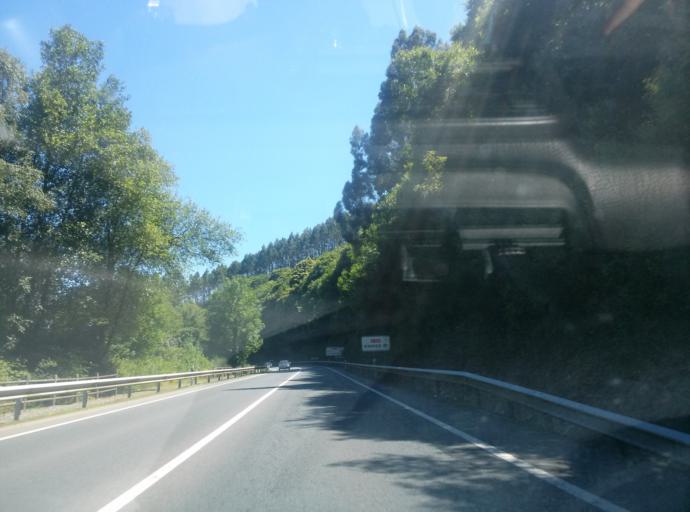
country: ES
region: Galicia
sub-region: Provincia de Lugo
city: Meira
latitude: 43.2174
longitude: -7.3132
